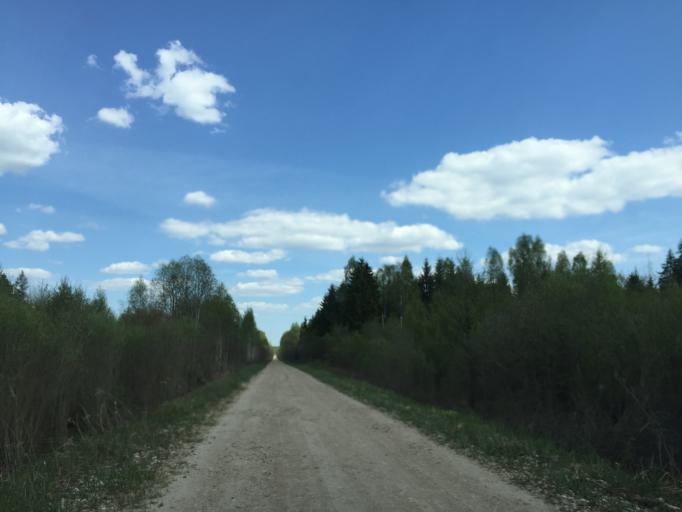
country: LV
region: Limbazu Rajons
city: Limbazi
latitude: 57.4027
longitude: 24.5989
